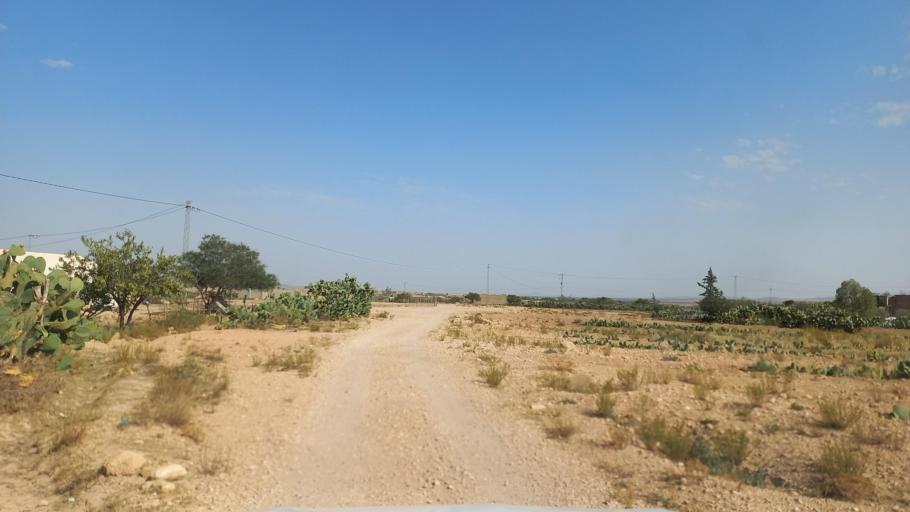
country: TN
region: Al Qasrayn
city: Kasserine
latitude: 35.2836
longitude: 8.9449
